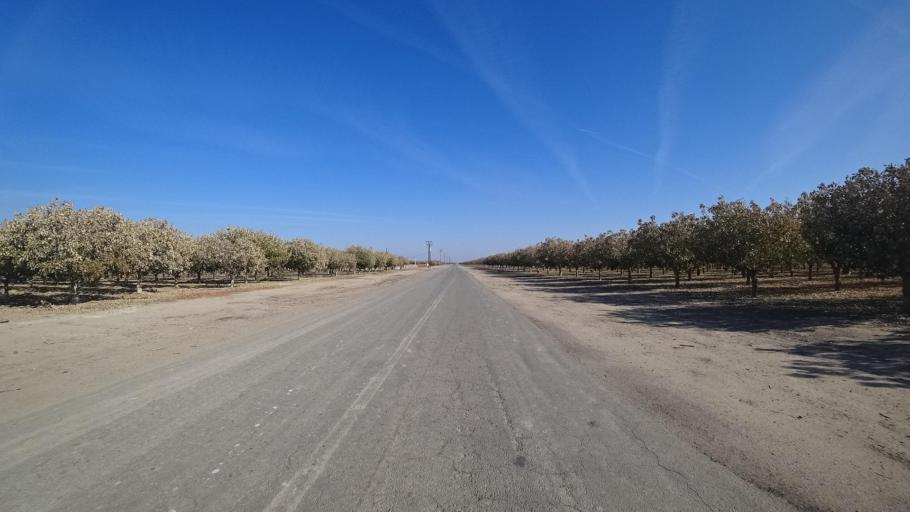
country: US
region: California
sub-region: Kern County
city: Wasco
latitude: 35.6886
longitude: -119.4302
